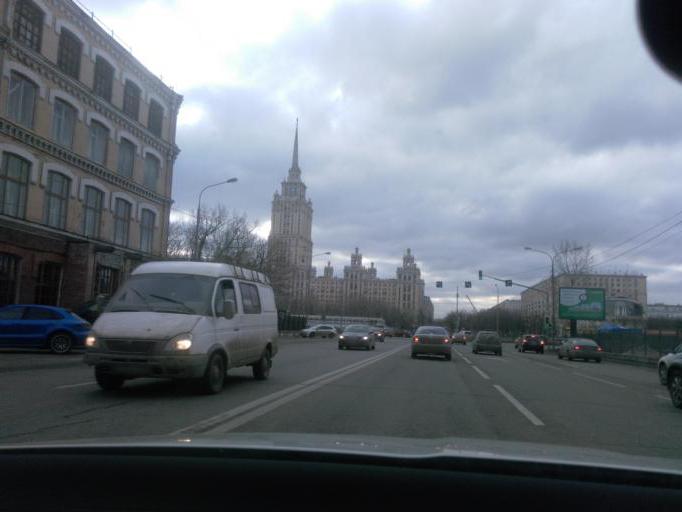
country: RU
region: Moskovskaya
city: Dorogomilovo
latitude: 55.7550
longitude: 37.5599
